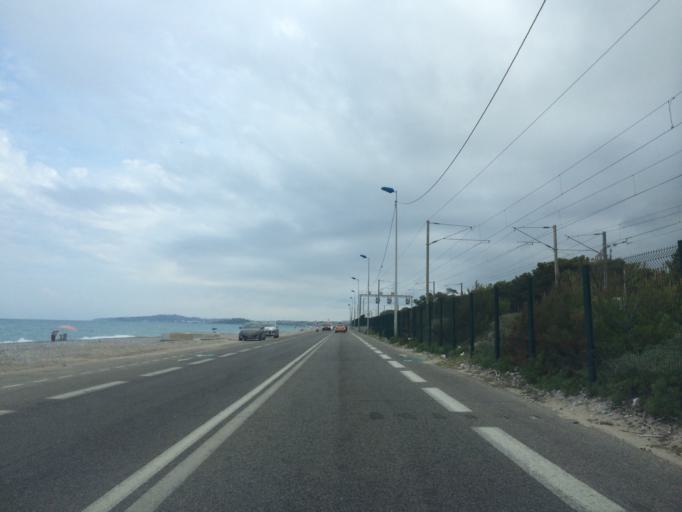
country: FR
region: Provence-Alpes-Cote d'Azur
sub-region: Departement des Alpes-Maritimes
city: Biot
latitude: 43.6257
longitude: 7.1329
